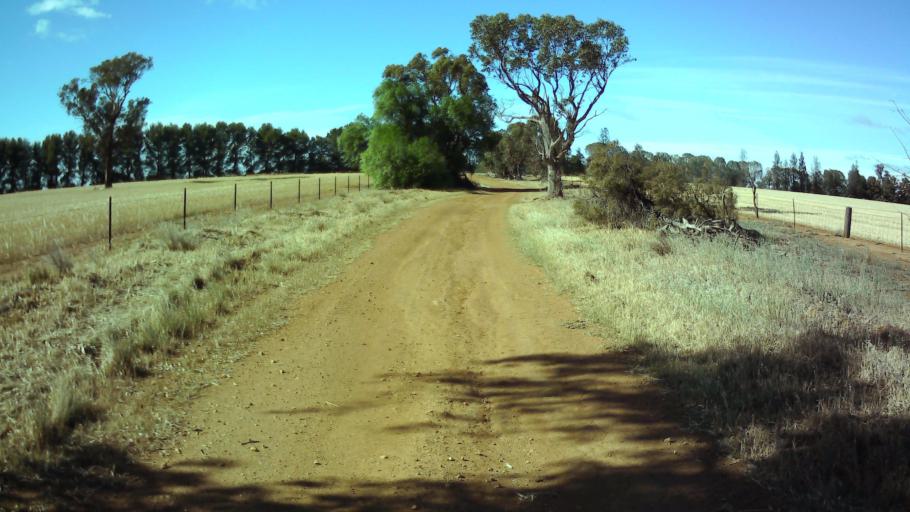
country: AU
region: New South Wales
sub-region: Weddin
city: Grenfell
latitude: -34.0599
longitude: 148.2674
